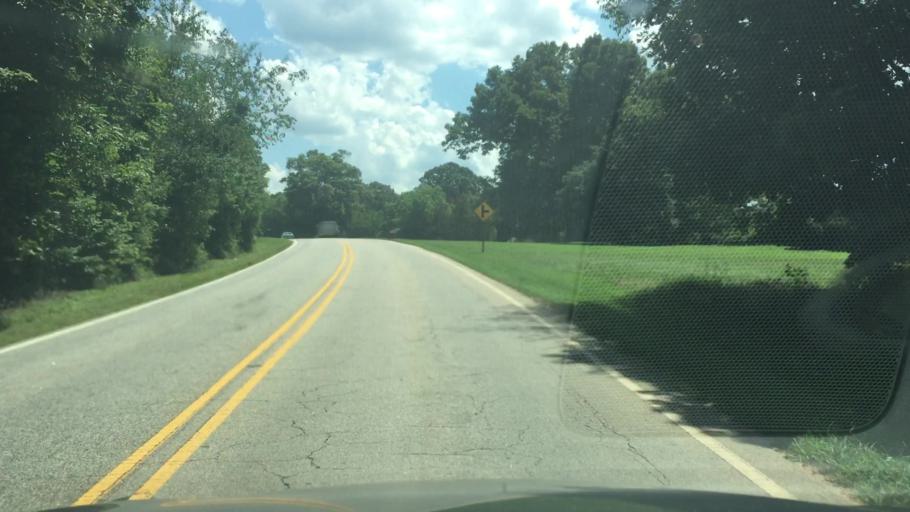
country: US
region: North Carolina
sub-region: Rowan County
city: Landis
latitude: 35.6144
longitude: -80.6533
